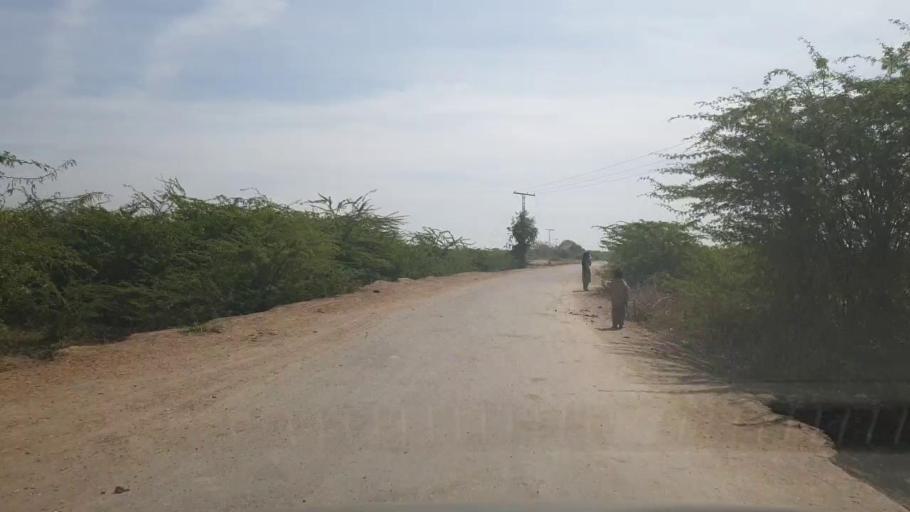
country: PK
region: Sindh
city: Umarkot
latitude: 25.3345
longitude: 69.5908
